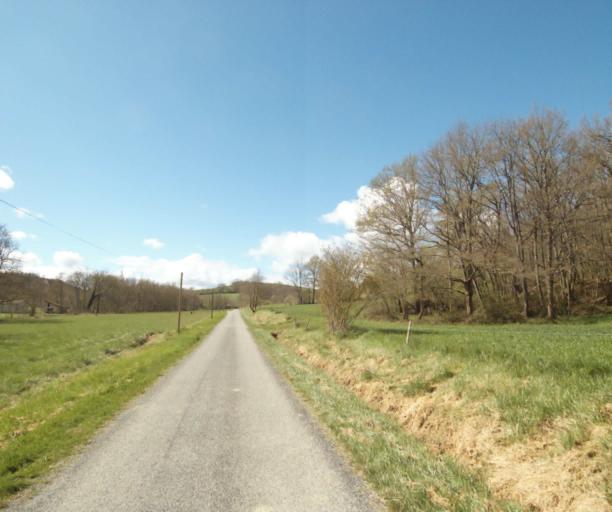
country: FR
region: Midi-Pyrenees
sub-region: Departement de l'Ariege
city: Saverdun
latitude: 43.1812
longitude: 1.5532
